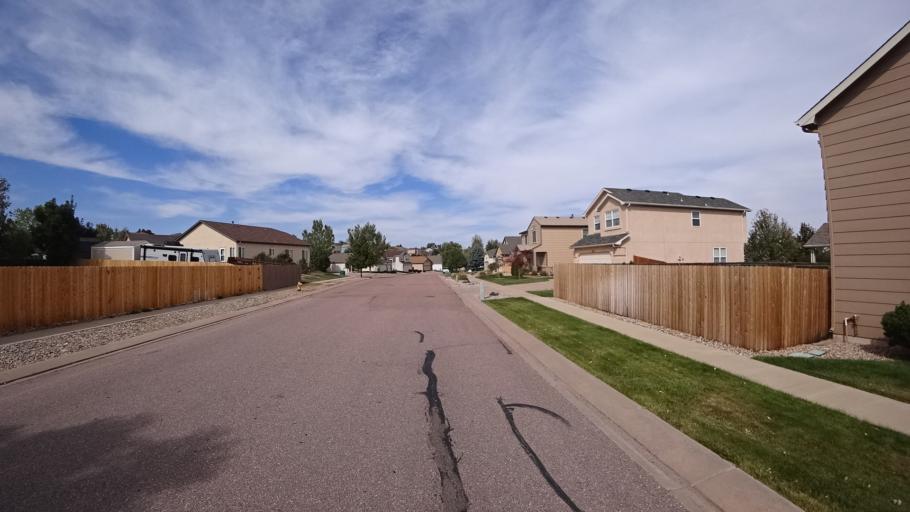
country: US
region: Colorado
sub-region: El Paso County
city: Cimarron Hills
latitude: 38.9017
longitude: -104.6897
